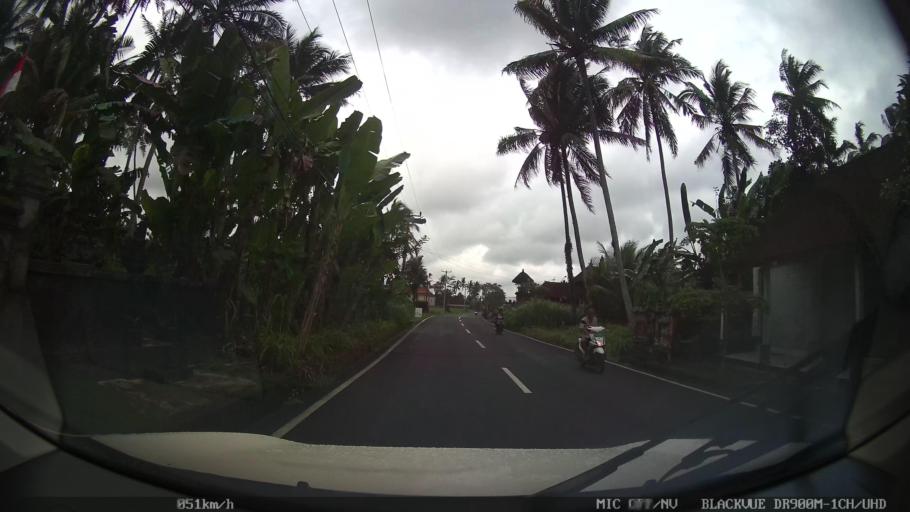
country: ID
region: Bali
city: Banjar Sayanbaleran
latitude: -8.5103
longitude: 115.1881
